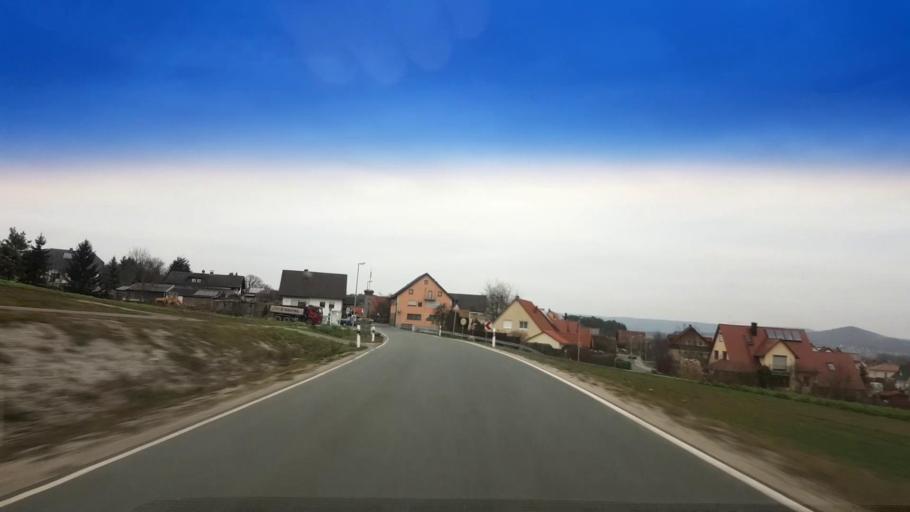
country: DE
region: Bavaria
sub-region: Upper Franconia
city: Hallerndorf
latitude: 49.7711
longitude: 10.9980
